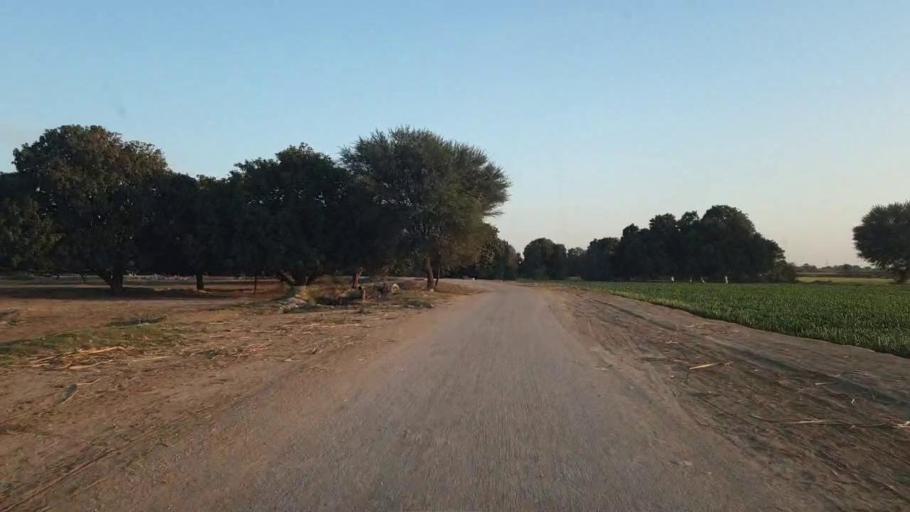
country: PK
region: Sindh
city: Tando Allahyar
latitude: 25.3712
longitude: 68.7497
